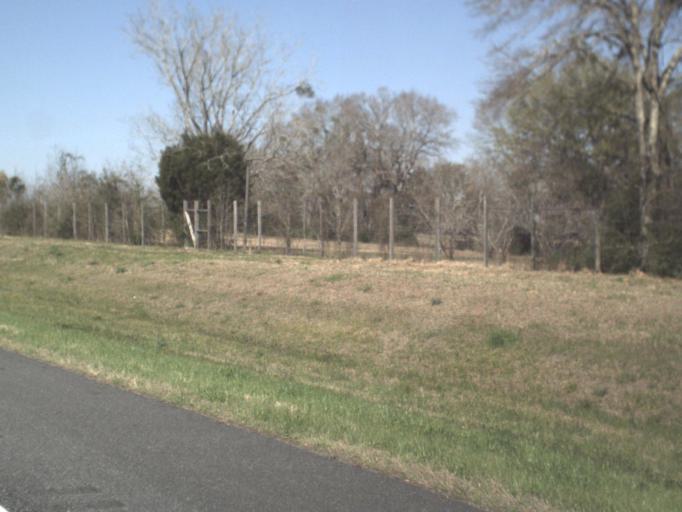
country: US
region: Florida
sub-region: Jackson County
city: Marianna
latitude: 30.7554
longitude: -85.3630
